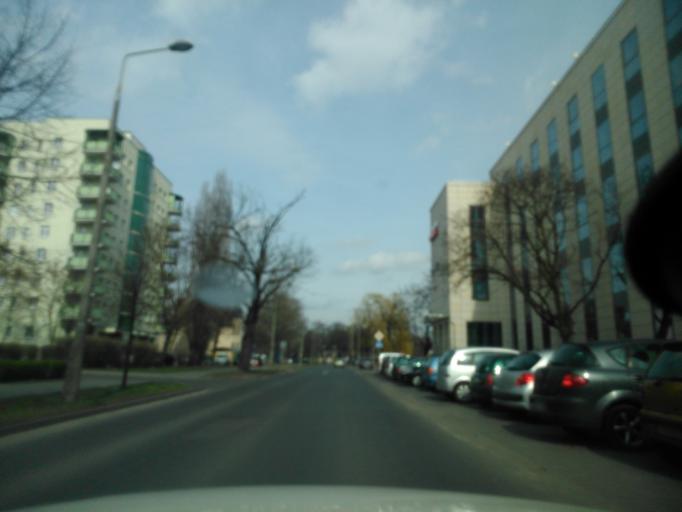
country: PL
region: Kujawsko-Pomorskie
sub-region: Torun
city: Torun
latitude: 53.0197
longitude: 18.6103
